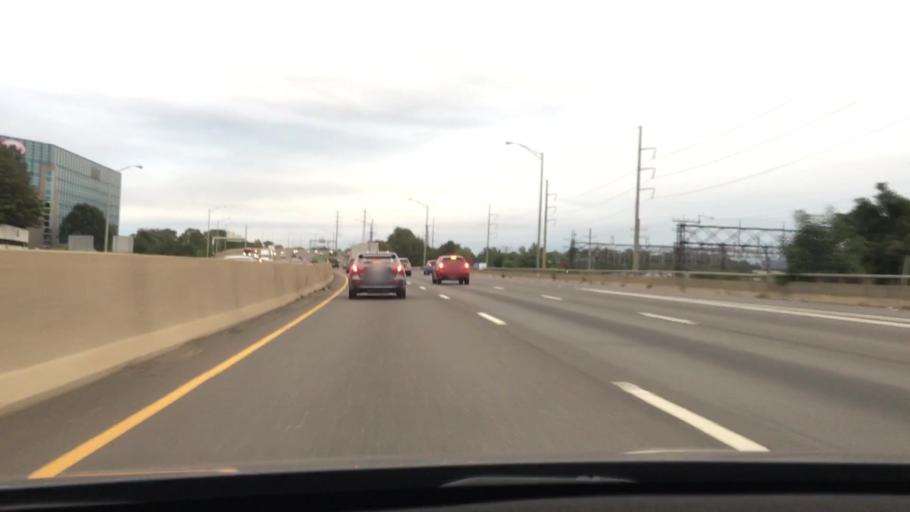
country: US
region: Connecticut
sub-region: Fairfield County
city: Stamford
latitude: 41.0500
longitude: -73.5327
